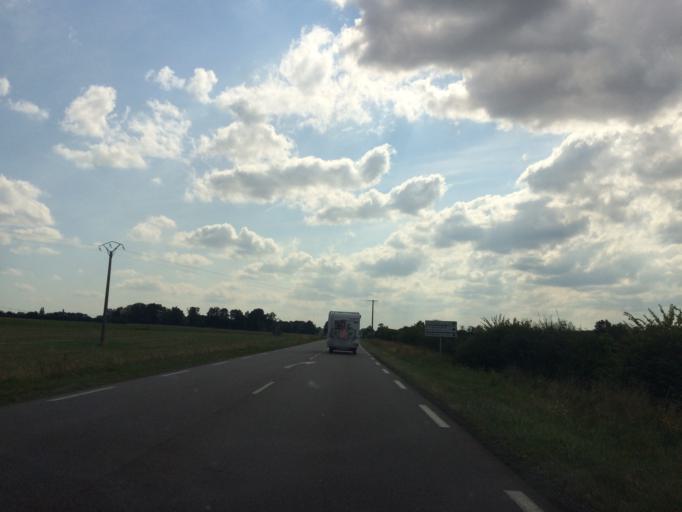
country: FR
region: Haute-Normandie
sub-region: Departement de l'Eure
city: Bourth
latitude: 48.6801
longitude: 0.8010
